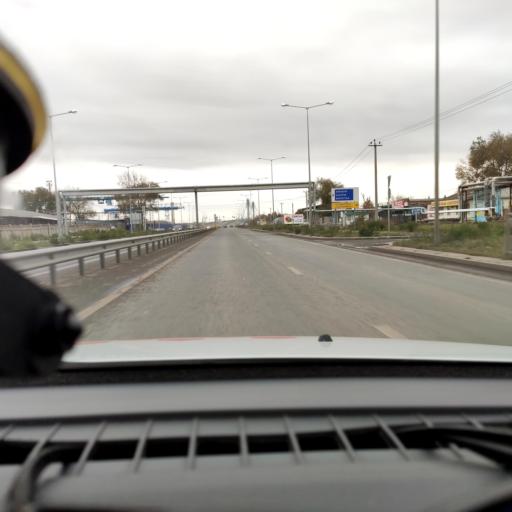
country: RU
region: Samara
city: Smyshlyayevka
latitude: 53.1887
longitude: 50.2981
